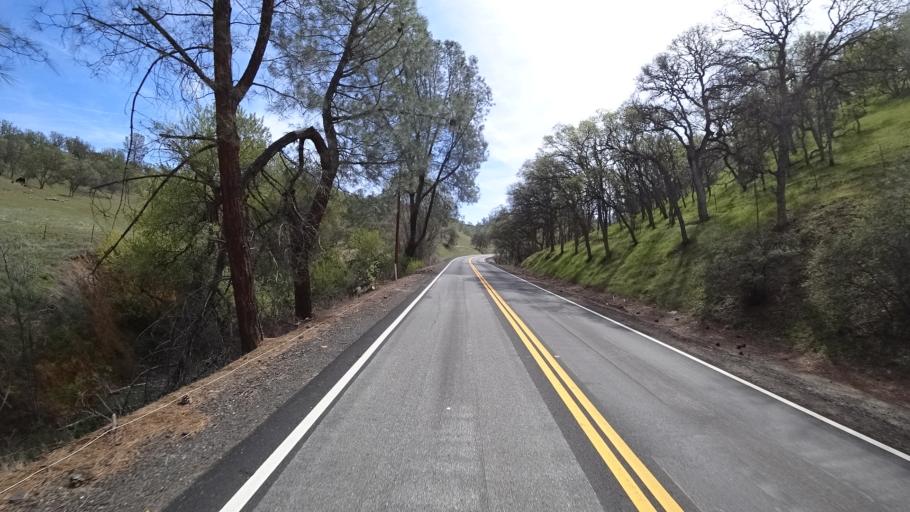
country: US
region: California
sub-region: Glenn County
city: Willows
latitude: 39.6150
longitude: -122.5118
